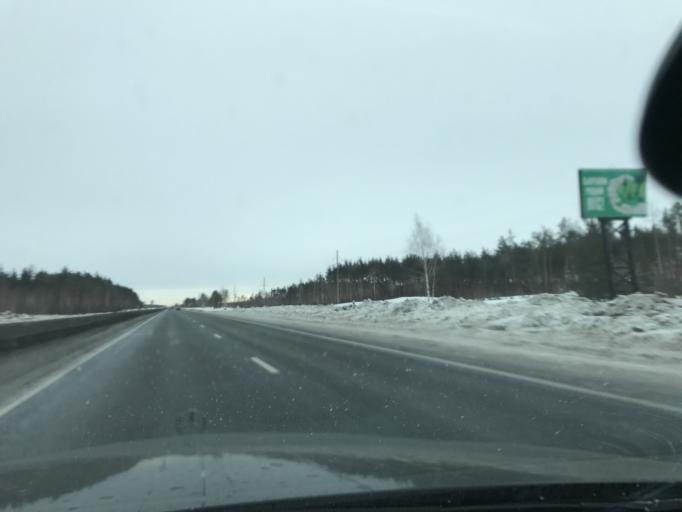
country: RU
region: Nizjnij Novgorod
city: Pyra
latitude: 56.2957
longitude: 43.4127
